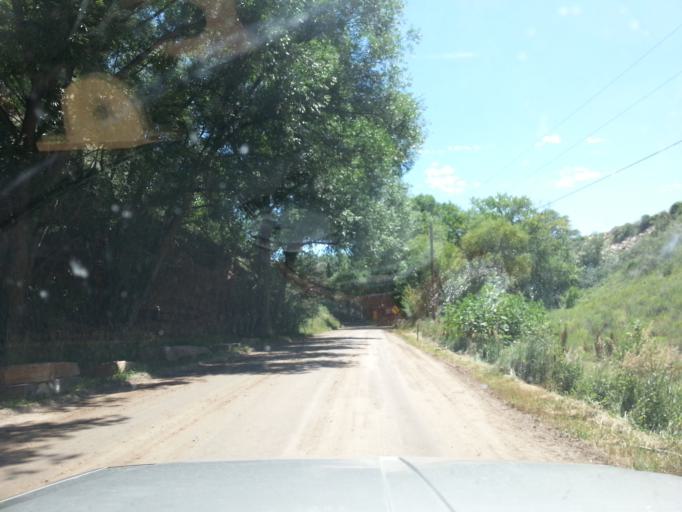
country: US
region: Colorado
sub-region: Larimer County
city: Loveland
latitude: 40.4795
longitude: -105.2173
